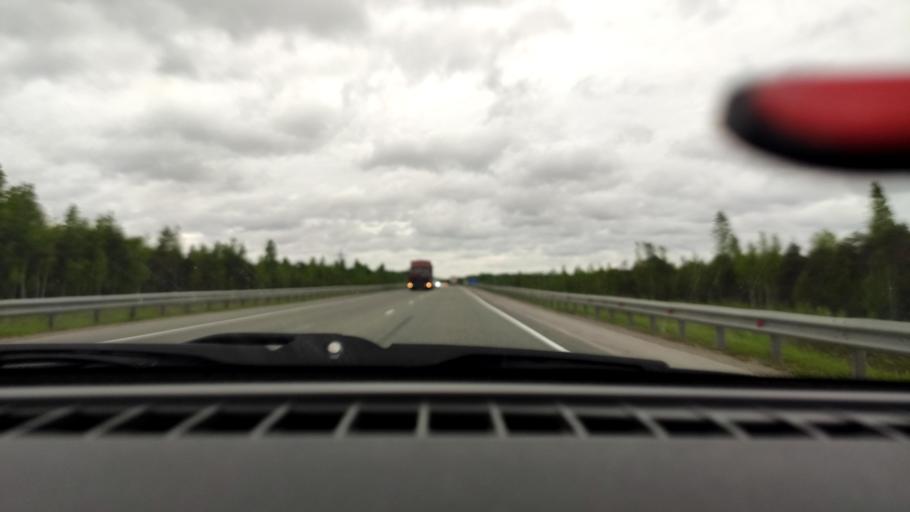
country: RU
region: Perm
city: Krasnokamsk
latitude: 58.1037
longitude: 55.7613
